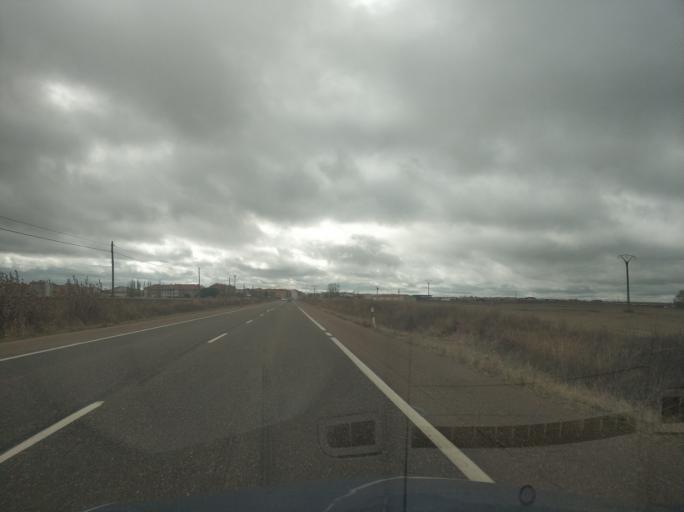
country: ES
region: Castille and Leon
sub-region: Provincia de Salamanca
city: Castellanos de Moriscos
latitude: 41.0247
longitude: -5.5871
